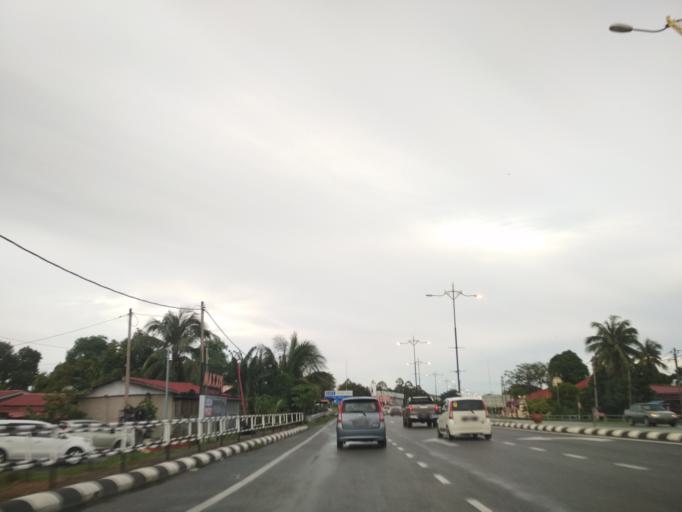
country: MY
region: Perlis
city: Kangar
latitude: 6.4349
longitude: 100.2026
